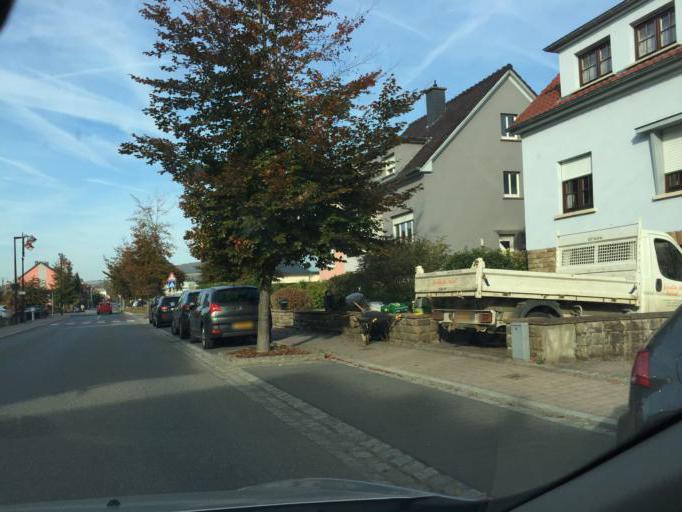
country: LU
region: Diekirch
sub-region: Canton de Diekirch
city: Diekirch
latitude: 49.8650
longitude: 6.1710
